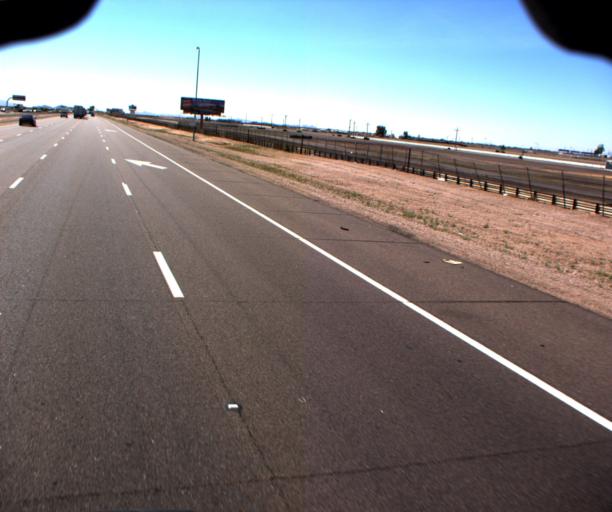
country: US
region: Arizona
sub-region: Maricopa County
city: Guadalupe
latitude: 33.2757
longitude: -111.9640
